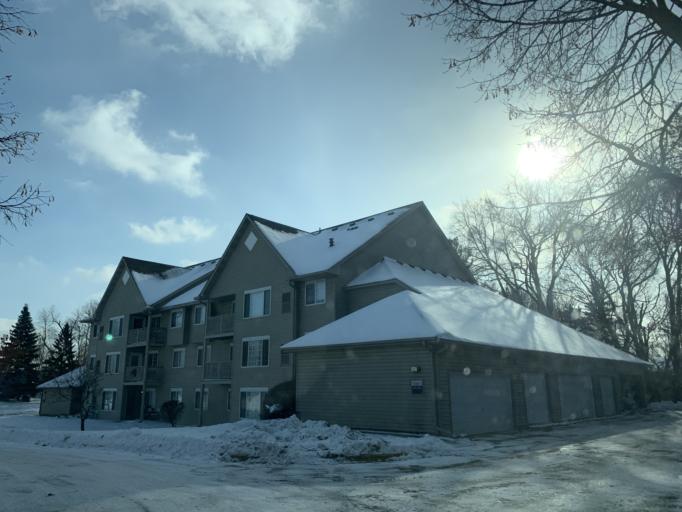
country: US
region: Minnesota
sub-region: Dakota County
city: Inver Grove Heights
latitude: 44.8717
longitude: -93.0661
